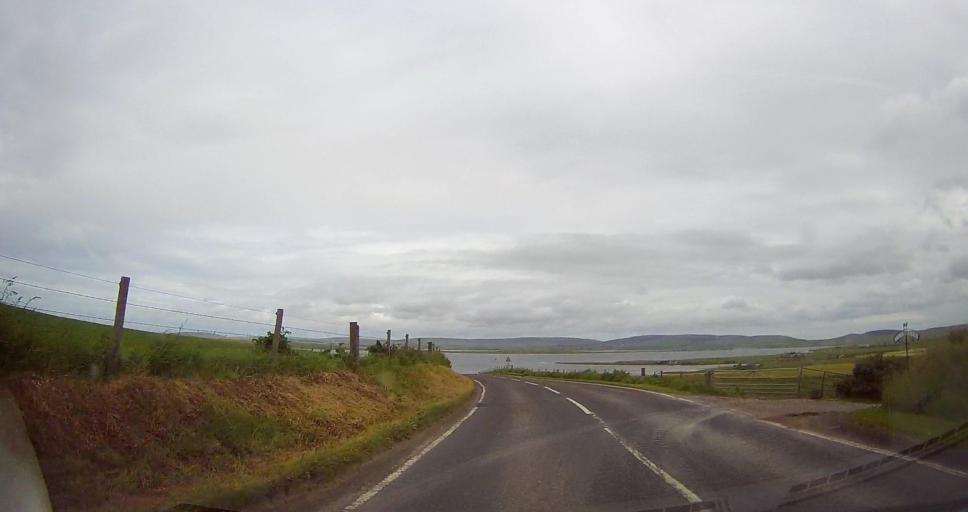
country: GB
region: Scotland
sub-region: Orkney Islands
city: Stromness
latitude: 58.9798
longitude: -3.2646
